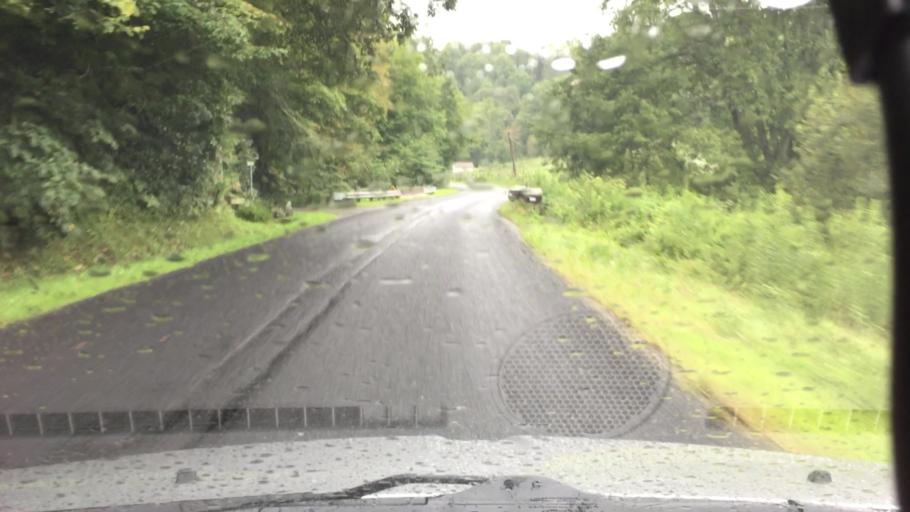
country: US
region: North Carolina
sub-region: Madison County
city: Mars Hill
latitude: 35.9112
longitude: -82.5204
